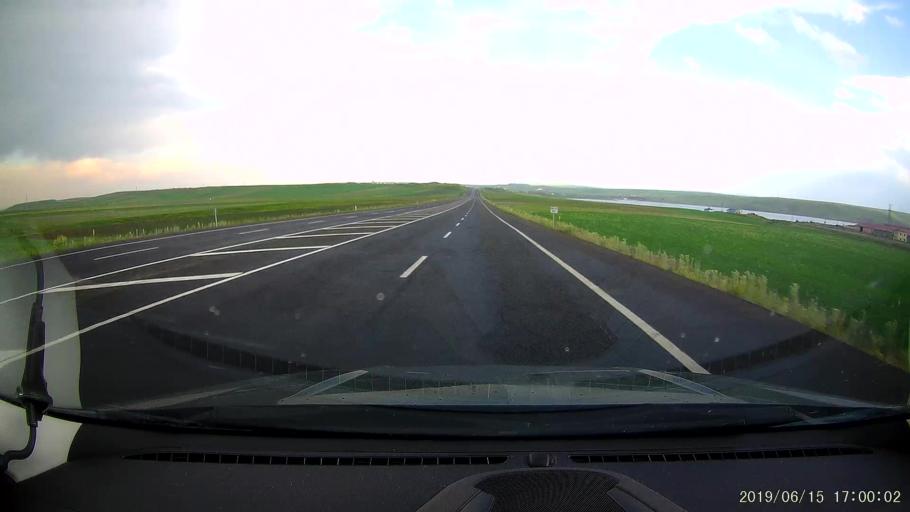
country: TR
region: Kars
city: Susuz
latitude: 40.7437
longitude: 43.1567
